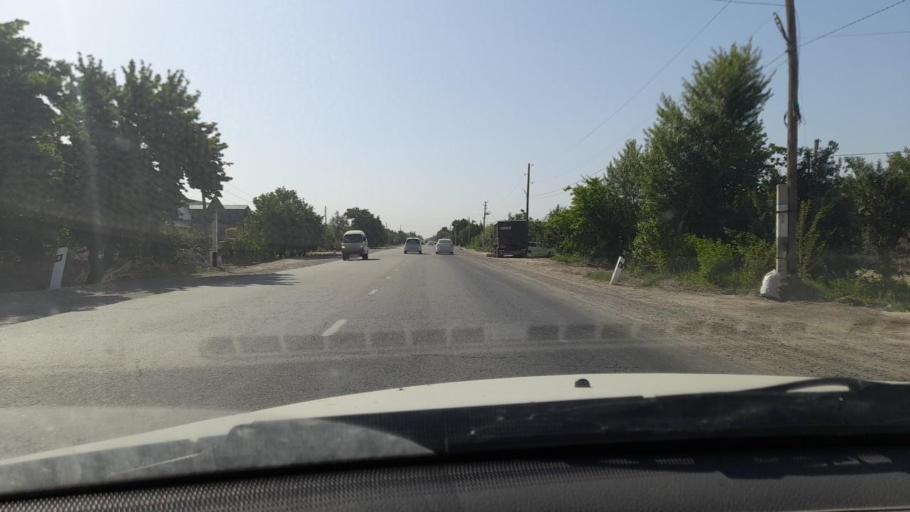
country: UZ
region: Bukhara
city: Romiton
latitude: 39.9095
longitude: 64.3971
